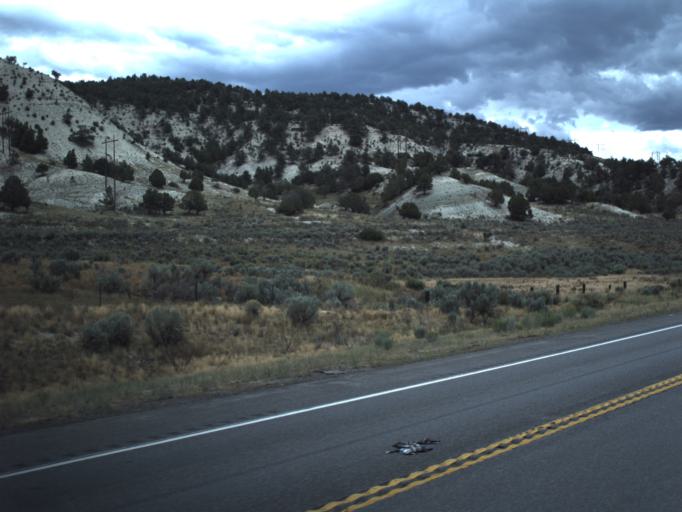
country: US
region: Utah
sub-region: Utah County
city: Mapleton
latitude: 39.9688
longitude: -111.3265
